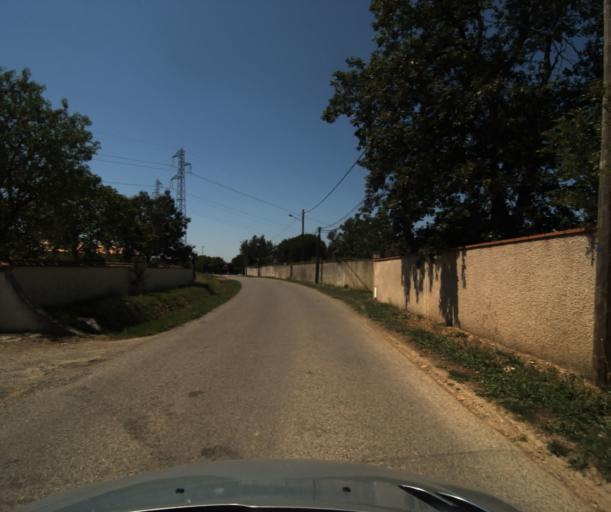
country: FR
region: Midi-Pyrenees
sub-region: Departement de la Haute-Garonne
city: Saubens
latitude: 43.4762
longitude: 1.3576
